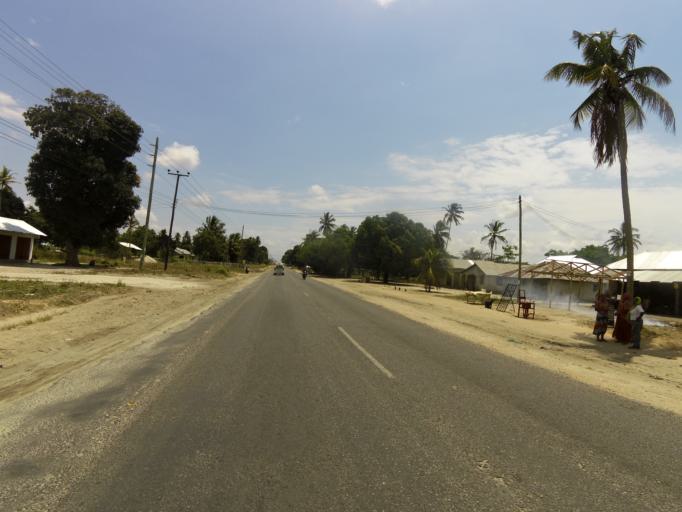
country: TZ
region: Pwani
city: Vikindu
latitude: -7.0331
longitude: 39.2861
